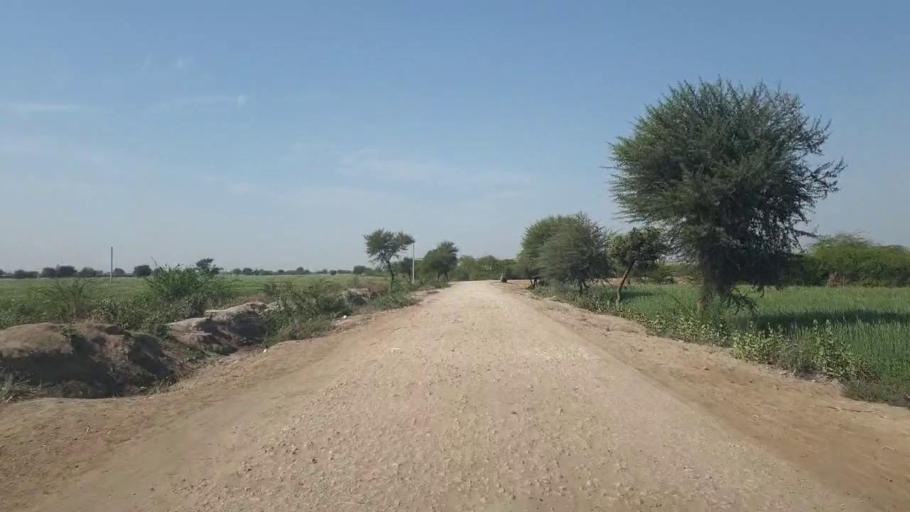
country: PK
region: Sindh
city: Umarkot
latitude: 25.2896
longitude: 69.6516
